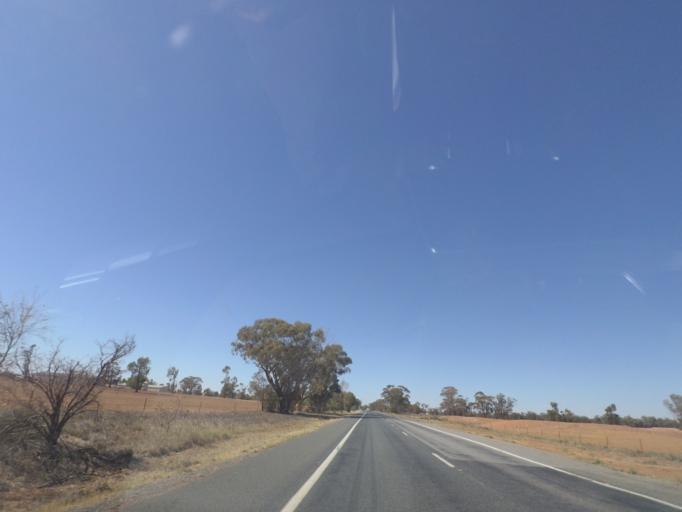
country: AU
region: New South Wales
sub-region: Bland
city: West Wyalong
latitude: -34.1900
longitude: 147.1118
